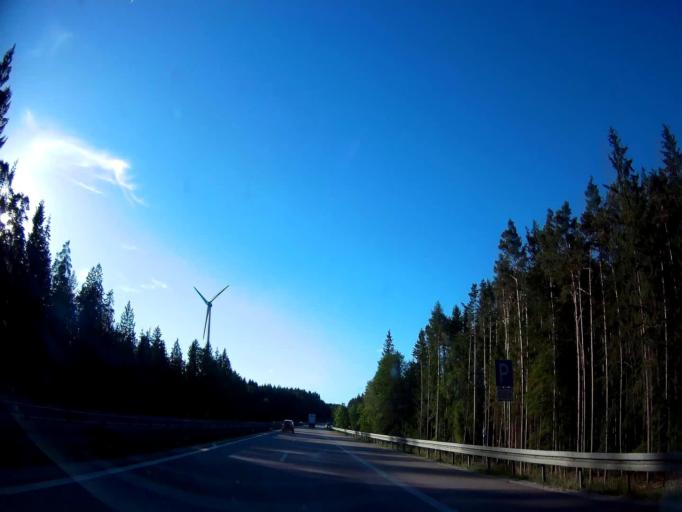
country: DE
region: Bavaria
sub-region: Upper Palatinate
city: Brunn
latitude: 49.1131
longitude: 11.8746
